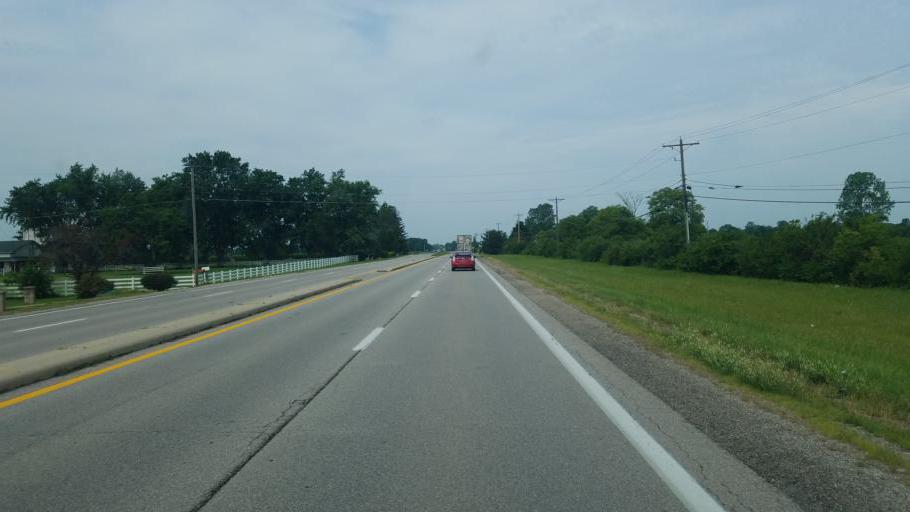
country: US
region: Ohio
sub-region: Franklin County
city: Lake Darby
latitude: 39.9469
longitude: -83.2439
